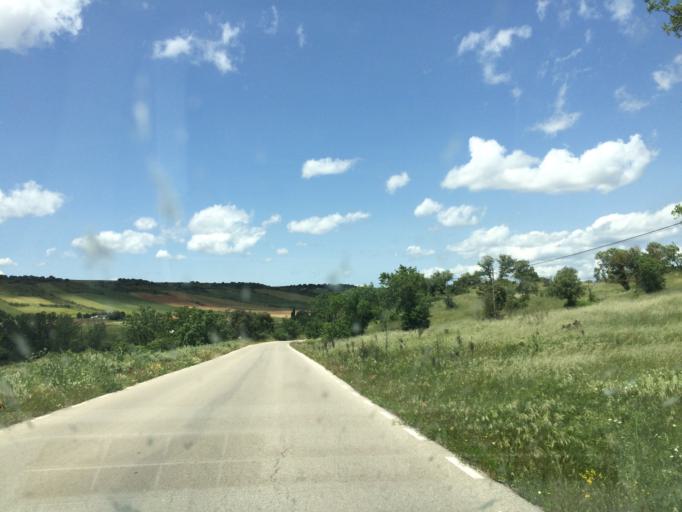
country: ES
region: Madrid
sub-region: Provincia de Madrid
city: Valdepielagos
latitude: 40.7602
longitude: -3.4139
